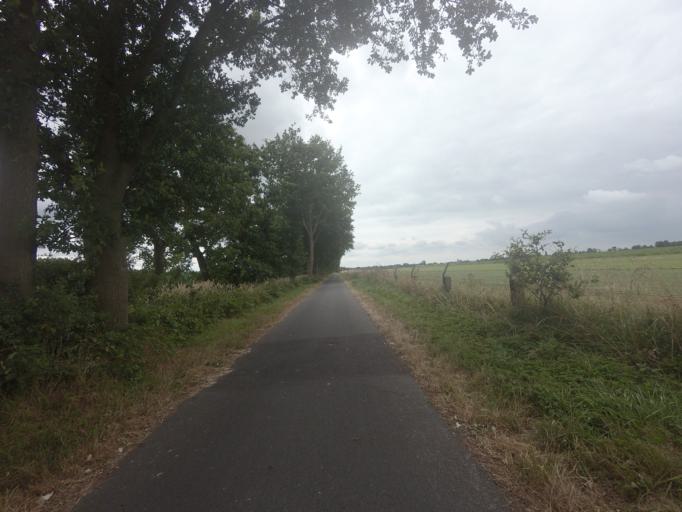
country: NL
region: North Holland
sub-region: Gemeente Wijdemeren
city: Nieuw-Loosdrecht
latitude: 52.1701
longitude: 5.1816
